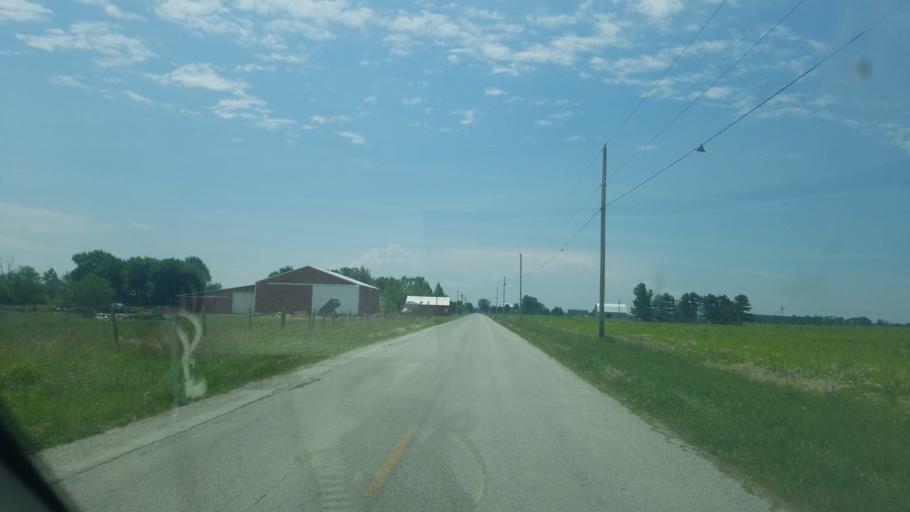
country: US
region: Ohio
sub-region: Wood County
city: North Baltimore
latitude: 41.2141
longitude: -83.5924
